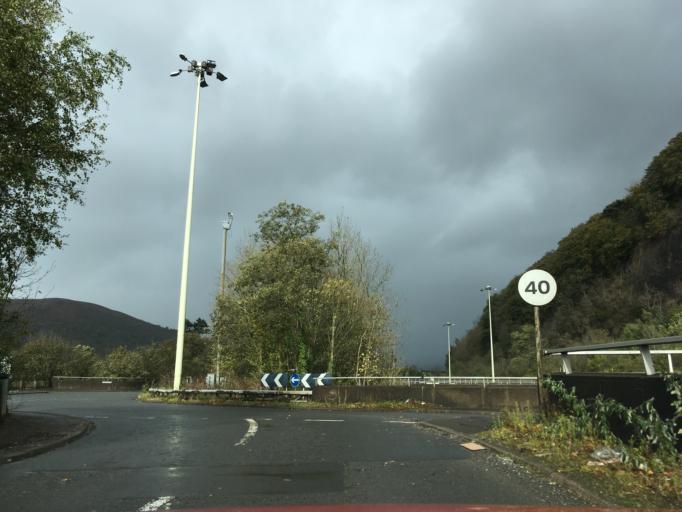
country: GB
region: Wales
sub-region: Cardiff
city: Radyr
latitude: 51.5359
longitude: -3.2588
